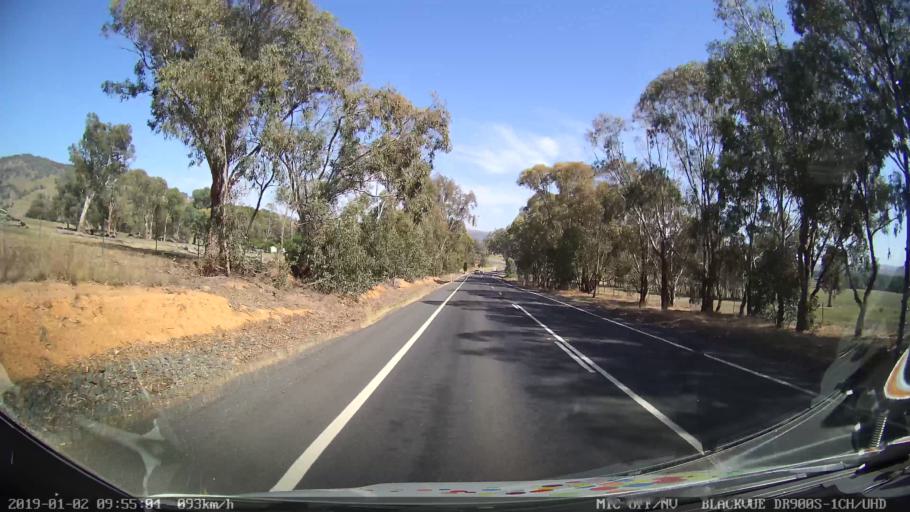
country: AU
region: New South Wales
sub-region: Tumut Shire
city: Tumut
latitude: -35.2274
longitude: 148.1925
